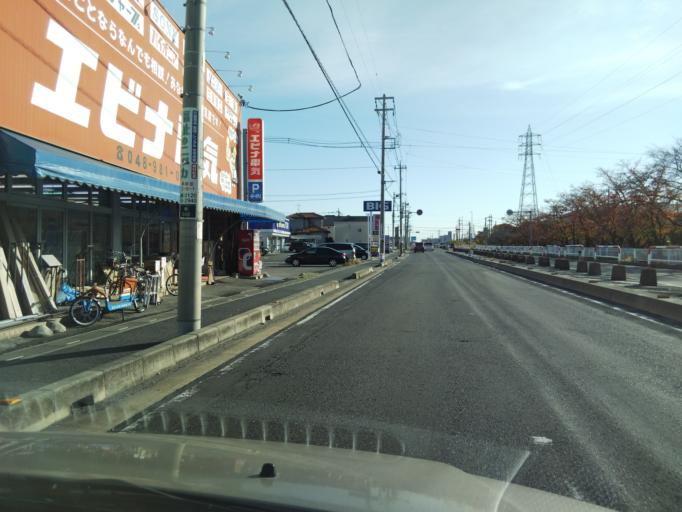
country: JP
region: Saitama
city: Yoshikawa
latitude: 35.8809
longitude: 139.8469
